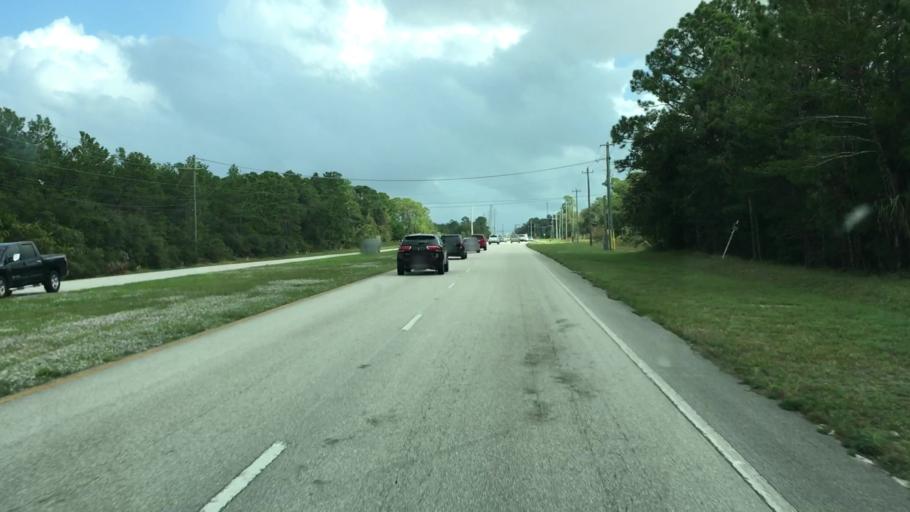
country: US
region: Florida
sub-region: Volusia County
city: Holly Hill
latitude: 29.2311
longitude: -81.0766
